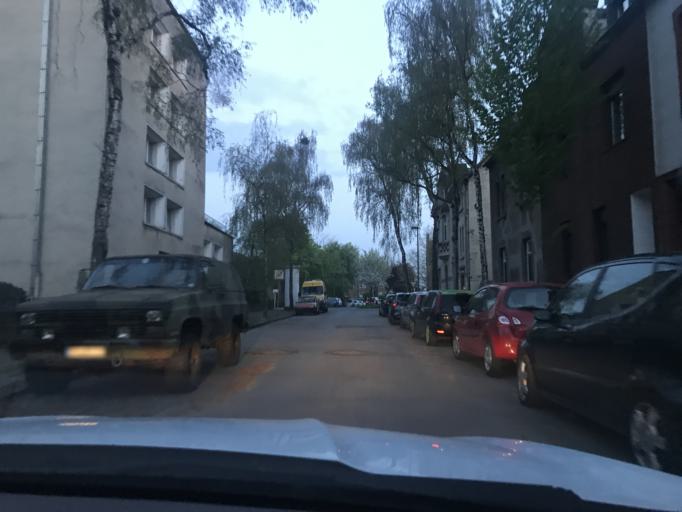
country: DE
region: North Rhine-Westphalia
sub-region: Regierungsbezirk Dusseldorf
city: Hochfeld
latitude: 51.3845
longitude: 6.7063
